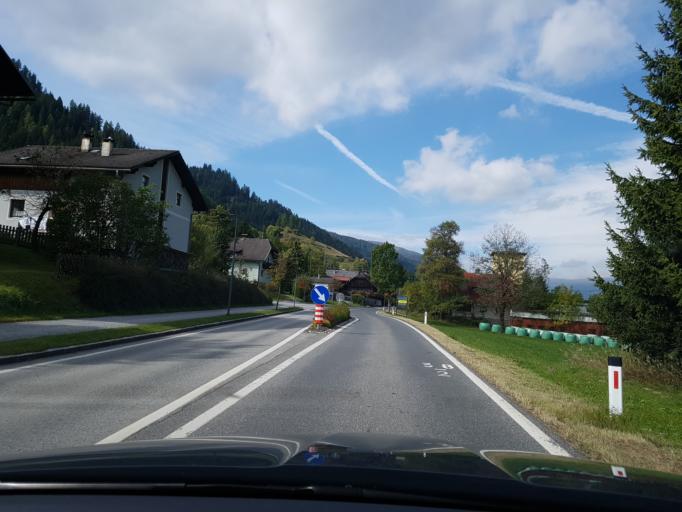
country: AT
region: Carinthia
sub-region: Politischer Bezirk Feldkirchen
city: Gnesau
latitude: 46.7763
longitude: 13.9590
